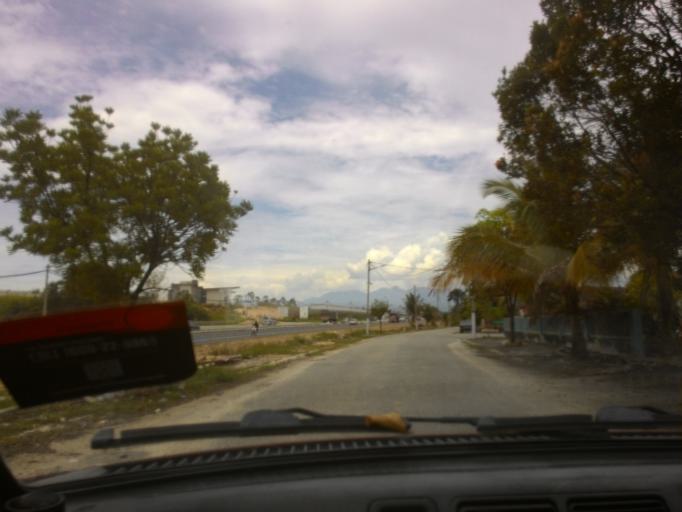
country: MY
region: Perak
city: Ipoh
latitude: 4.6789
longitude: 101.0799
